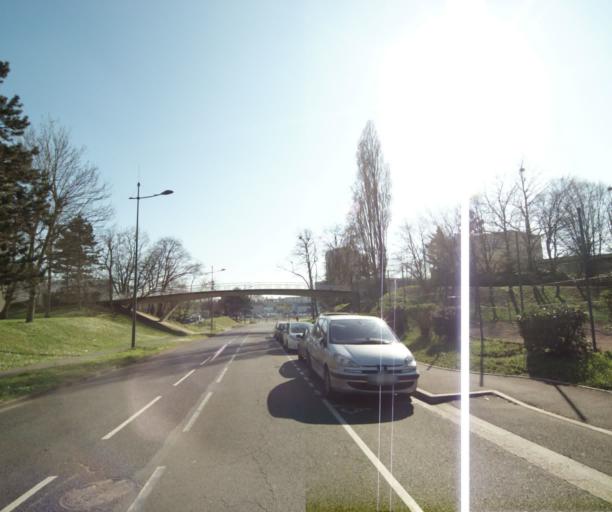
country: FR
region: Ile-de-France
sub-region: Departement du Val-d'Oise
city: Cergy
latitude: 49.0320
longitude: 2.0841
